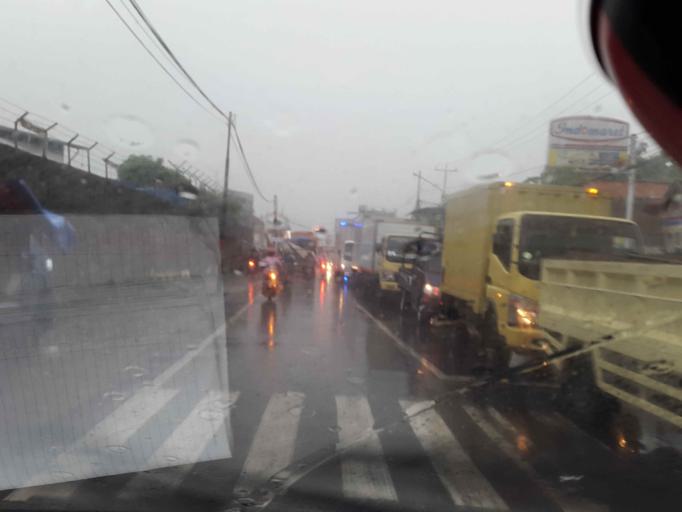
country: ID
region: West Java
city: Padalarang
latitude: -6.8638
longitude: 107.5033
